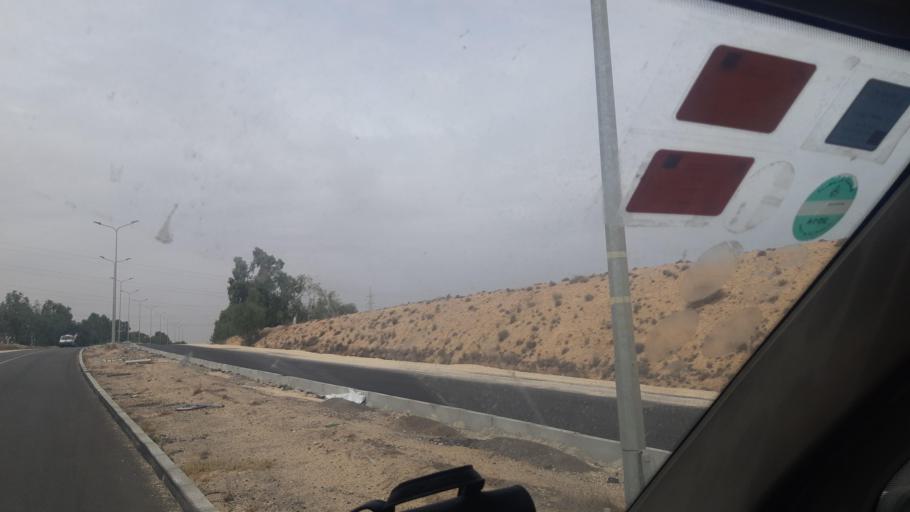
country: TN
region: Qabis
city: Gabes
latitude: 33.8548
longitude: 10.0310
